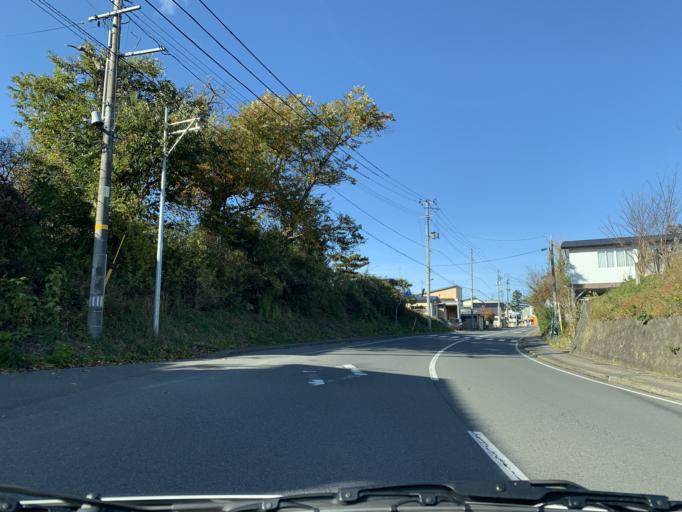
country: JP
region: Iwate
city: Mizusawa
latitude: 39.1933
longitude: 141.1192
